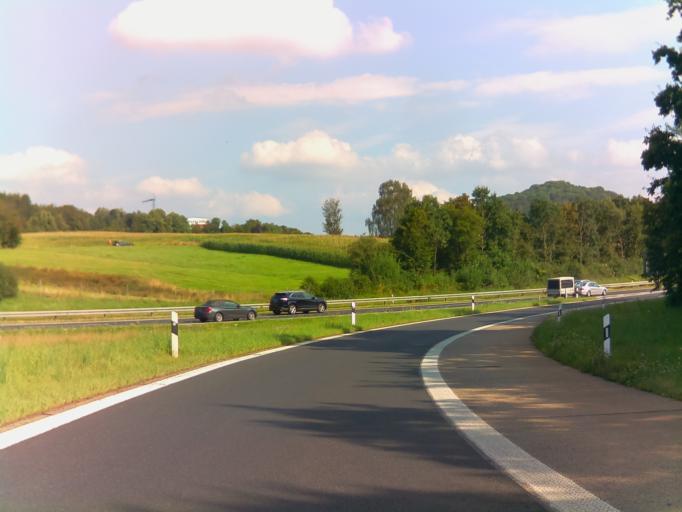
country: DE
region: Bavaria
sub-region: Regierungsbezirk Unterfranken
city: Riedenberg
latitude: 50.2948
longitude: 9.8488
